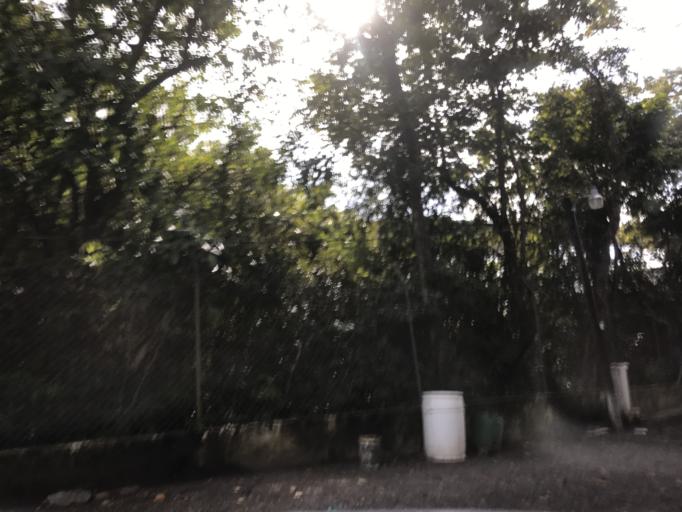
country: GT
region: Izabal
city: Morales
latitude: 15.6569
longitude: -88.9975
